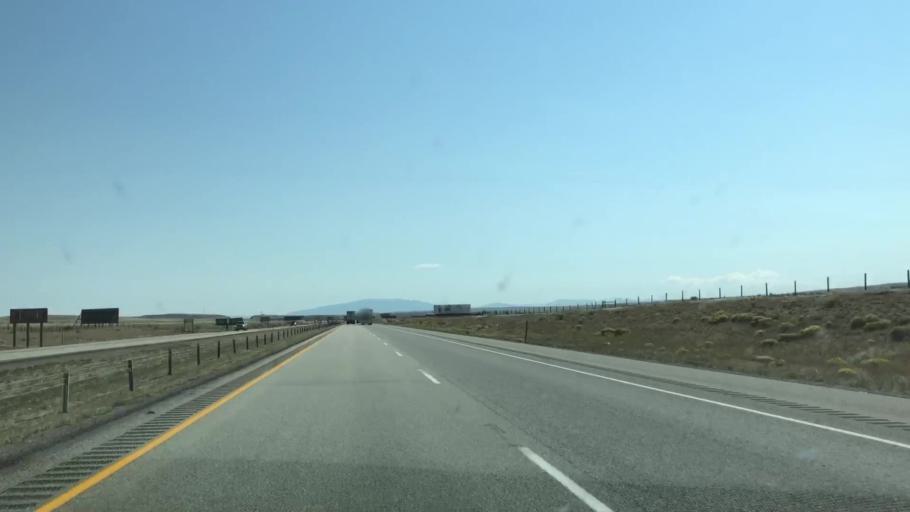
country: US
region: Wyoming
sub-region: Carbon County
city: Rawlins
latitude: 41.7869
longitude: -107.1870
